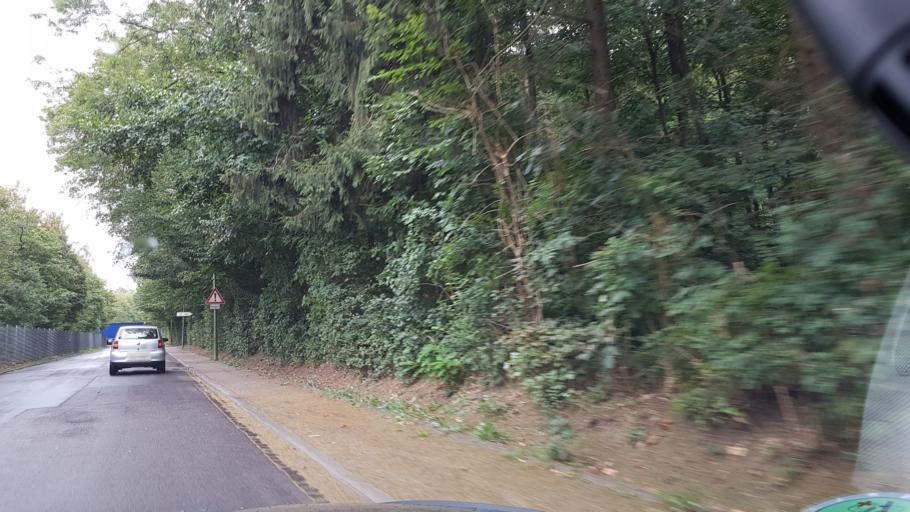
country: DE
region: Saarland
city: Sulzbach
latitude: 49.2889
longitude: 7.0662
